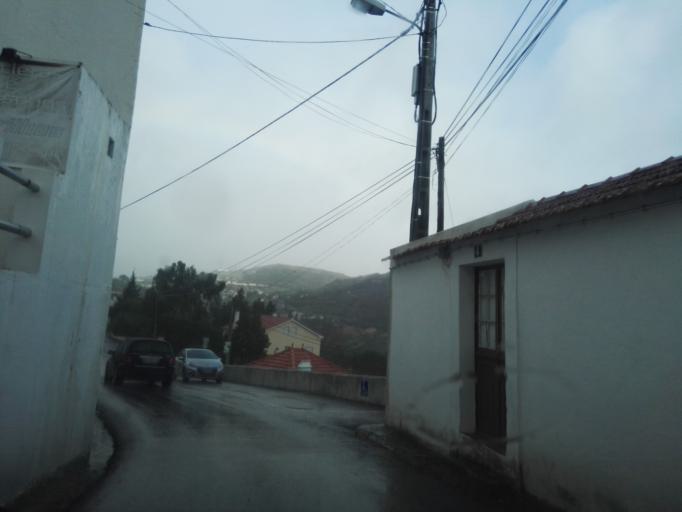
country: PT
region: Lisbon
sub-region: Vila Franca de Xira
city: Sobralinho
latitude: 38.9250
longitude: -9.0659
